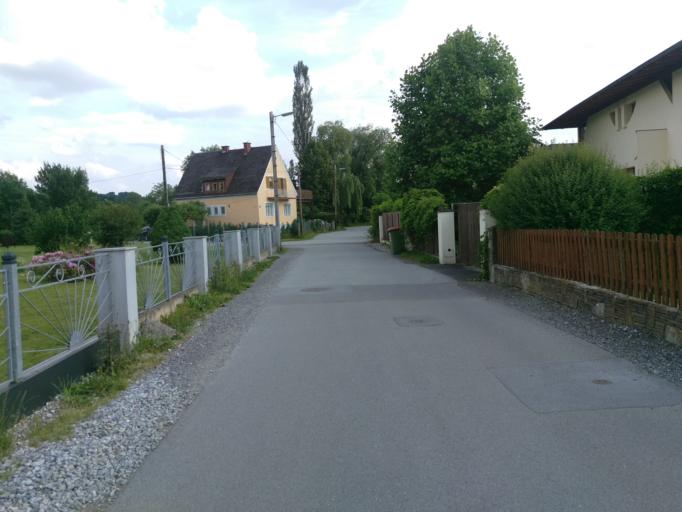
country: AT
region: Styria
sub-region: Politischer Bezirk Graz-Umgebung
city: Stattegg
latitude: 47.1105
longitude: 15.4253
